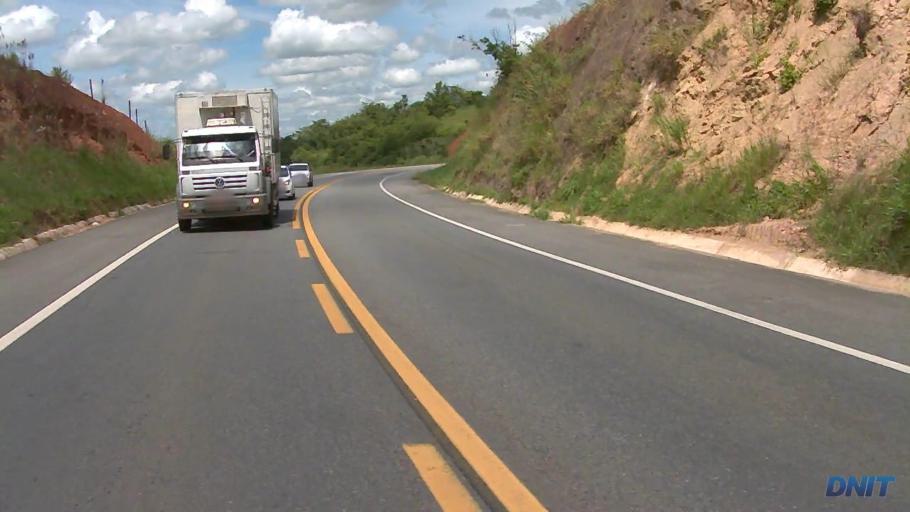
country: BR
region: Minas Gerais
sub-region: Governador Valadares
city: Governador Valadares
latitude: -18.9045
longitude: -42.0033
